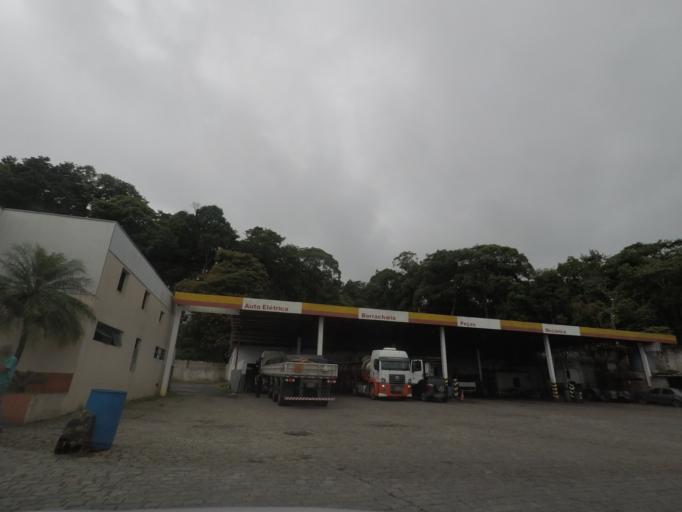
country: BR
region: Sao Paulo
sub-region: Jacupiranga
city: Jacupiranga
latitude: -24.6517
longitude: -47.9401
